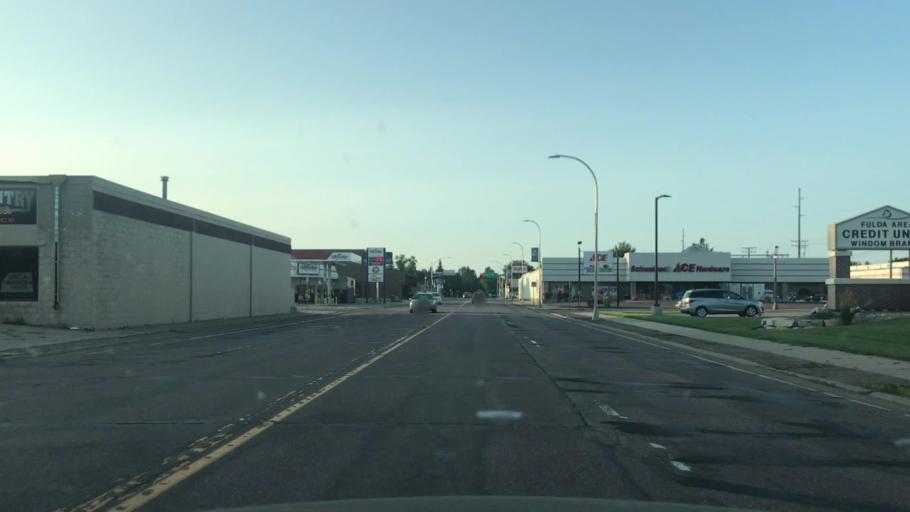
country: US
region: Minnesota
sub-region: Cottonwood County
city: Windom
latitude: 43.8647
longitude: -95.1149
